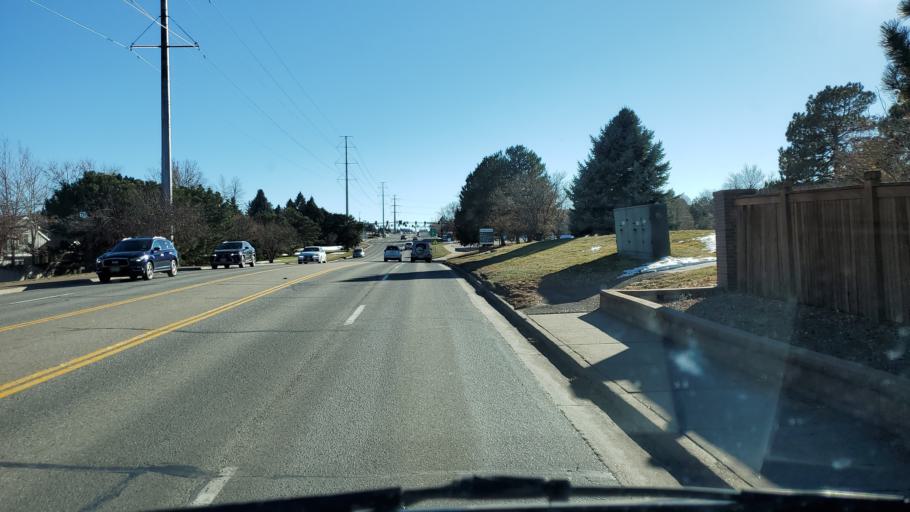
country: US
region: Colorado
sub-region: Arapahoe County
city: Castlewood
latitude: 39.5716
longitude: -104.9044
